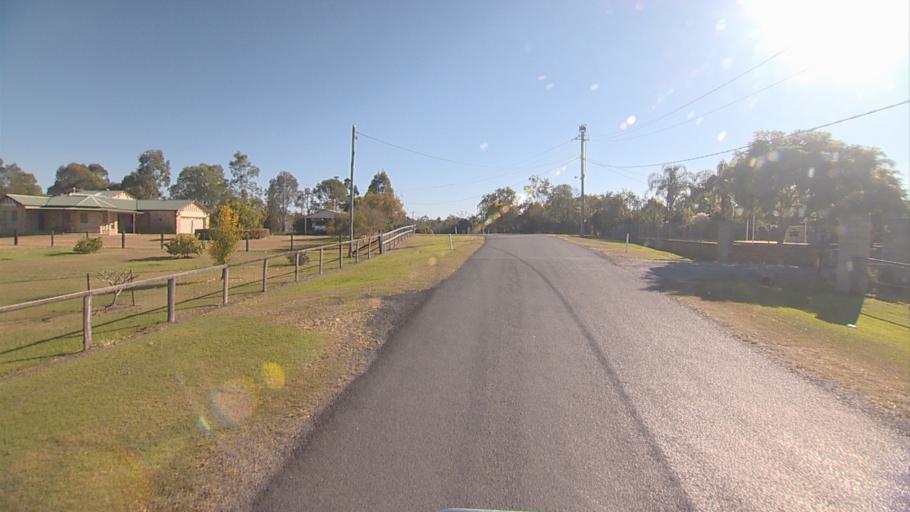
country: AU
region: Queensland
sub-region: Logan
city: North Maclean
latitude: -27.7911
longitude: 153.0262
